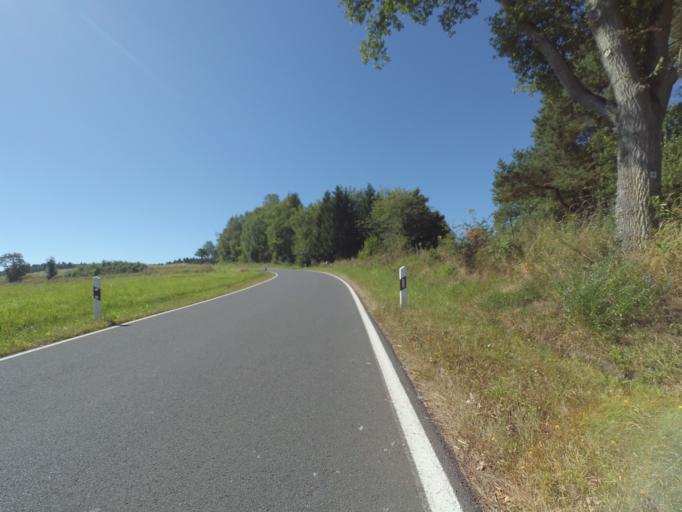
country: DE
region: Rheinland-Pfalz
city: Demerath
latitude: 50.1989
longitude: 6.9546
